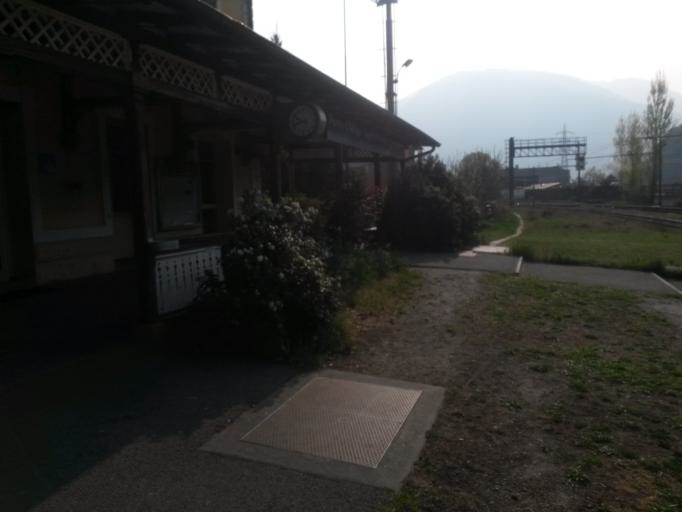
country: IT
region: Trentino-Alto Adige
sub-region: Bolzano
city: Cornaiano
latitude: 46.4856
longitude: 11.2977
